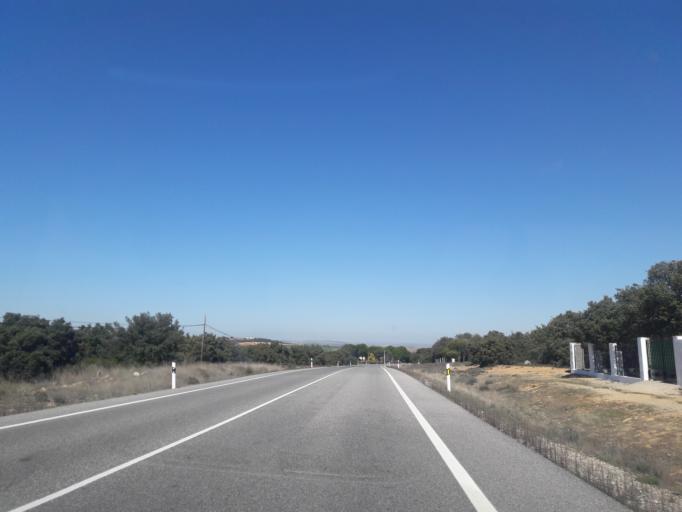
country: ES
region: Castille and Leon
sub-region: Provincia de Salamanca
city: Mozarbez
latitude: 40.8242
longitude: -5.6373
